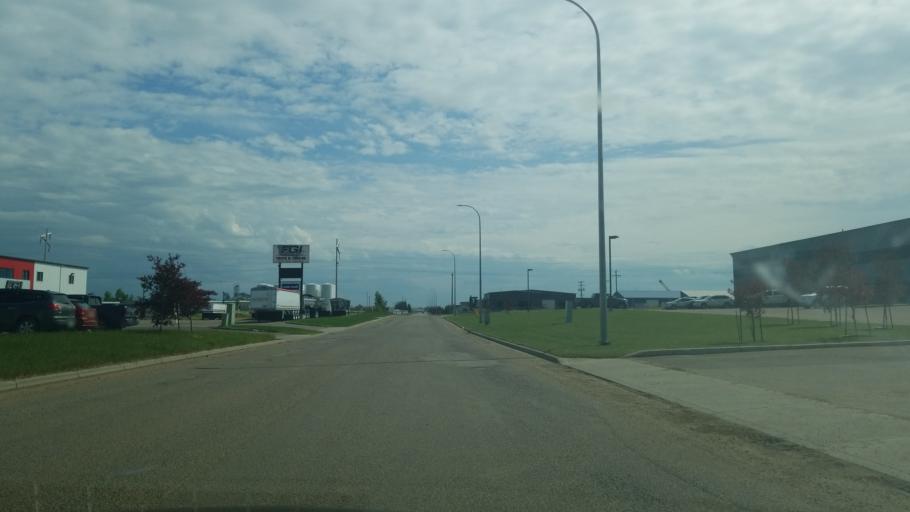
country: CA
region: Saskatchewan
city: Lloydminster
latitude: 53.2942
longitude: -110.0367
